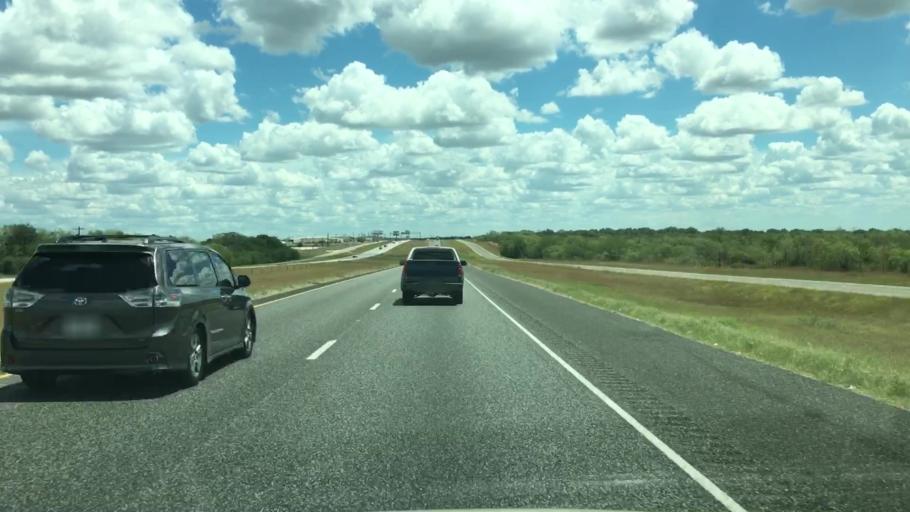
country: US
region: Texas
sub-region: Atascosa County
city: Pleasanton
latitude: 28.8977
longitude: -98.4175
